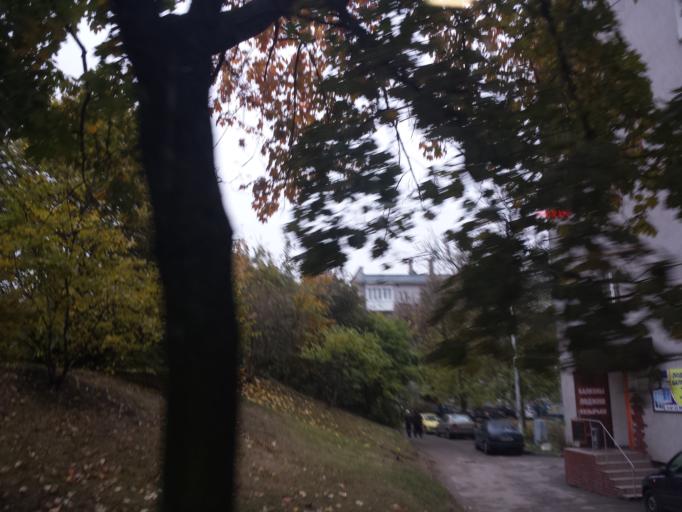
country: RU
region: Kaliningrad
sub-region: Gorod Kaliningrad
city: Kaliningrad
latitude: 54.6963
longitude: 20.5009
